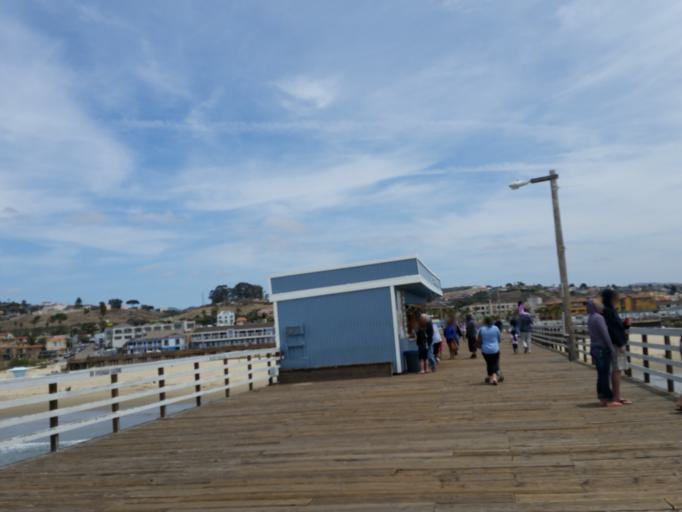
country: US
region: California
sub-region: San Luis Obispo County
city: Pismo Beach
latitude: 35.1380
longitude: -120.6455
